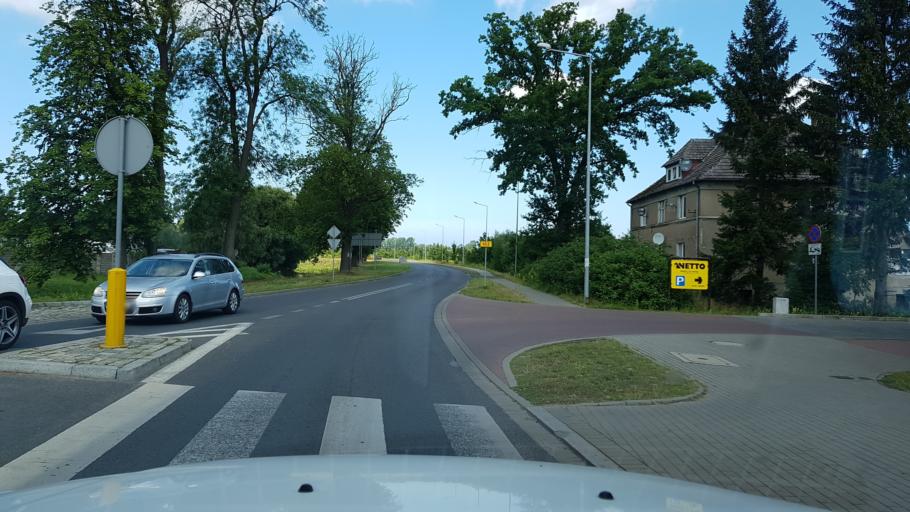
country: PL
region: West Pomeranian Voivodeship
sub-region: Powiat gryficki
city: Trzebiatow
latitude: 54.0651
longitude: 15.2731
